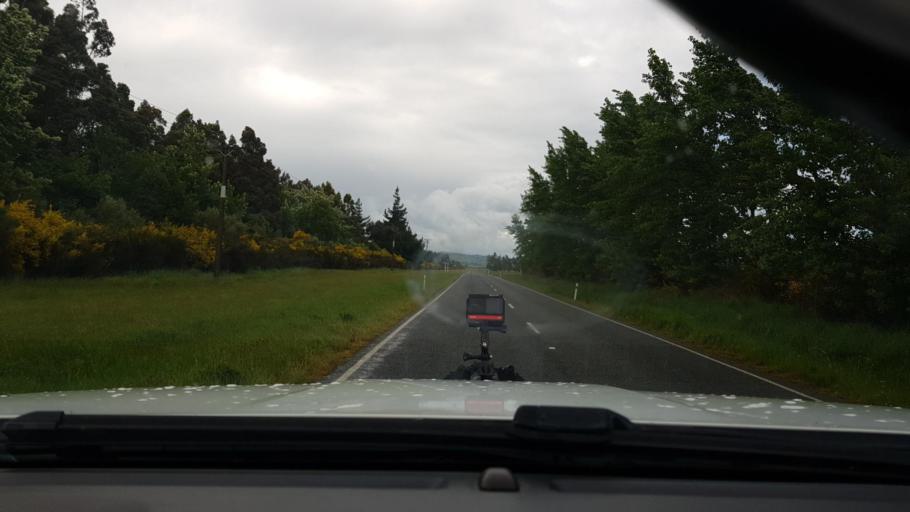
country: NZ
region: Southland
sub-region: Southland District
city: Winton
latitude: -45.7298
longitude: 168.3938
